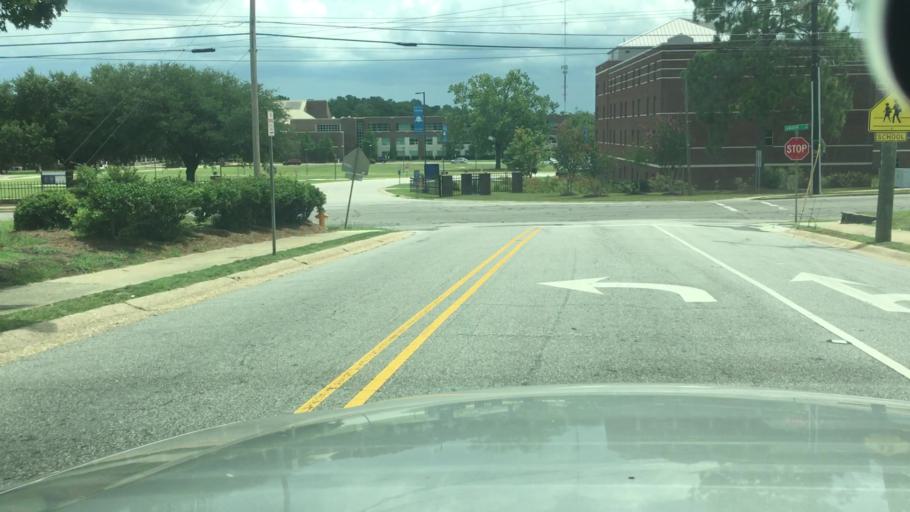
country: US
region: North Carolina
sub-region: Cumberland County
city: Fayetteville
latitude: 35.0784
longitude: -78.8934
